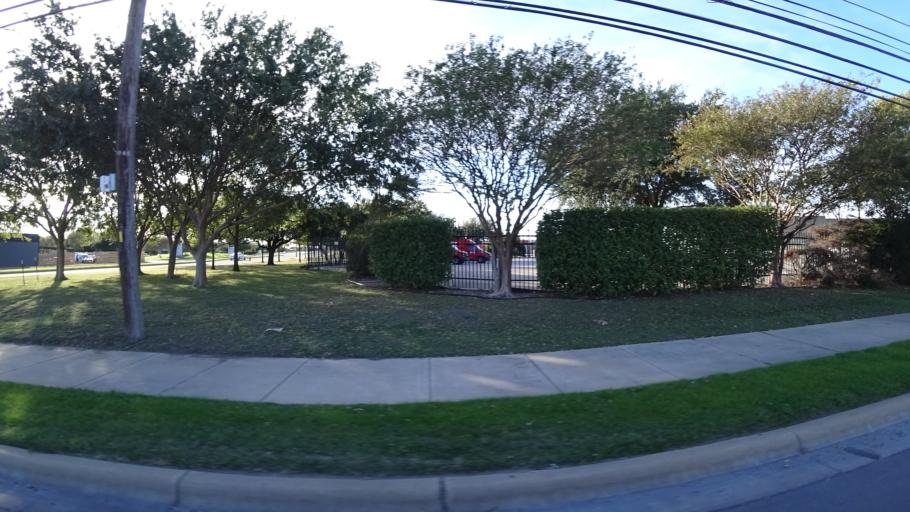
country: US
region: Texas
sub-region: Williamson County
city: Jollyville
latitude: 30.3778
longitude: -97.7255
